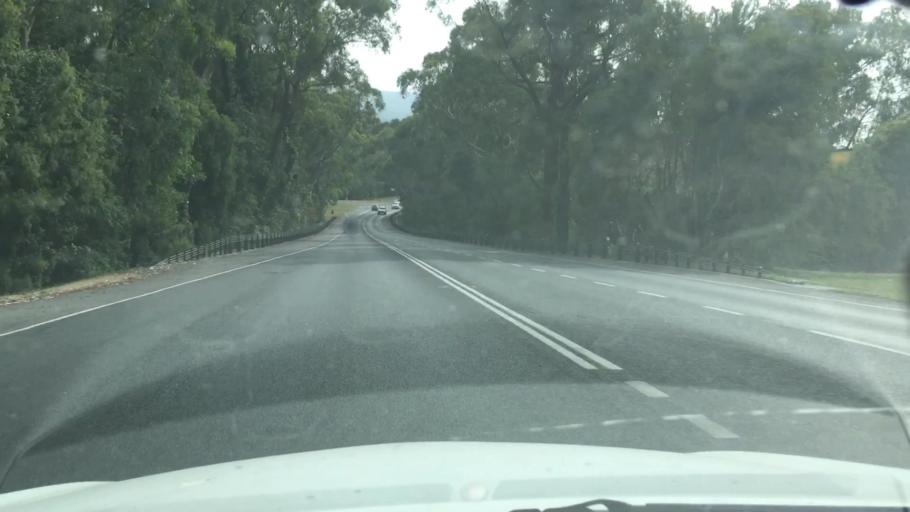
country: AU
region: Victoria
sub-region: Yarra Ranges
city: Launching Place
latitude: -37.7829
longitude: 145.5630
